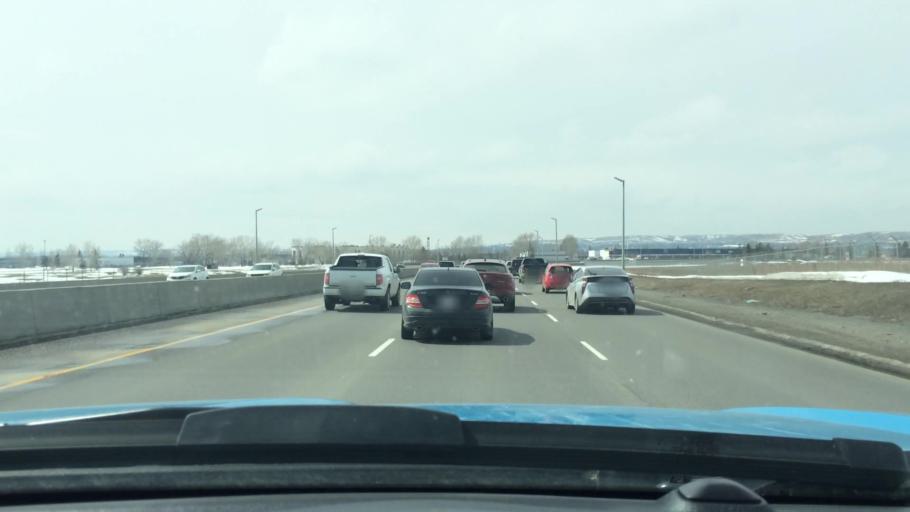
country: CA
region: Alberta
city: Calgary
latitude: 51.0930
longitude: -114.0196
